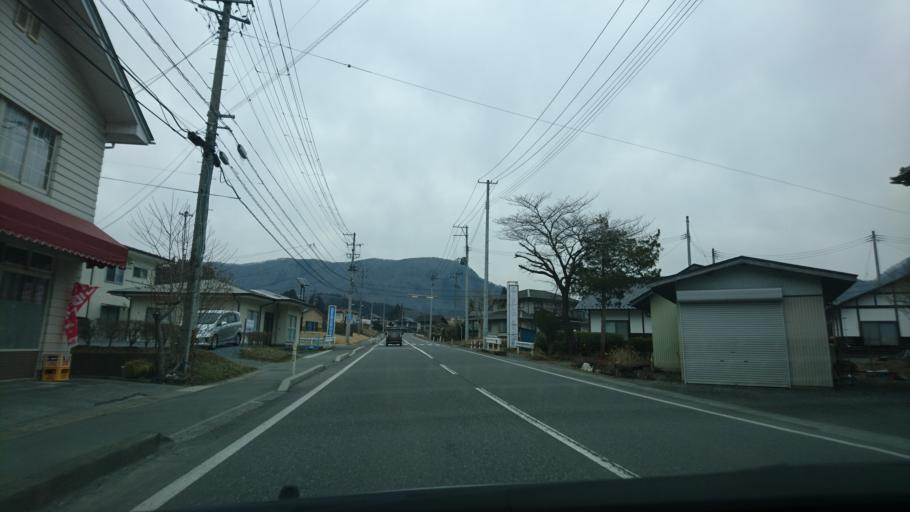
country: JP
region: Iwate
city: Tono
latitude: 39.1862
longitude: 141.5572
